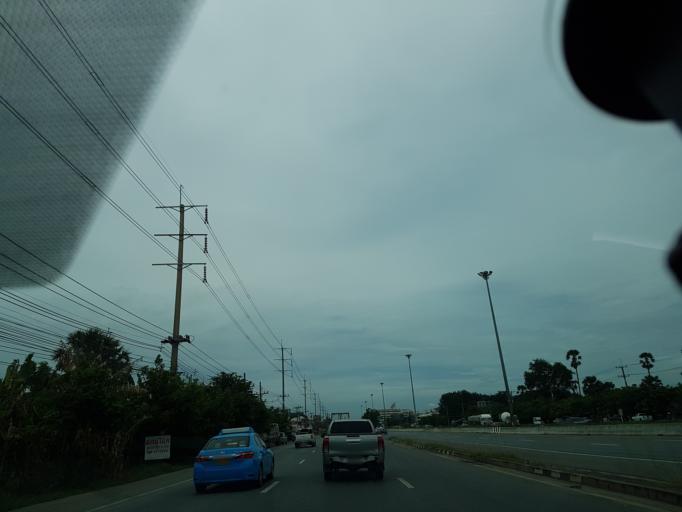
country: TH
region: Phra Nakhon Si Ayutthaya
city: Ban Bang Kadi Pathum Thani
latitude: 14.0203
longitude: 100.5530
